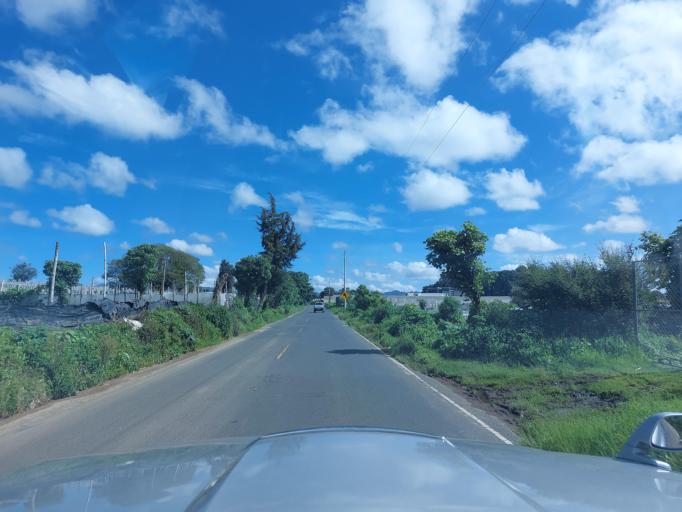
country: GT
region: Chimaltenango
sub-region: Municipio de Zaragoza
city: Zaragoza
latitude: 14.6634
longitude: -90.8992
